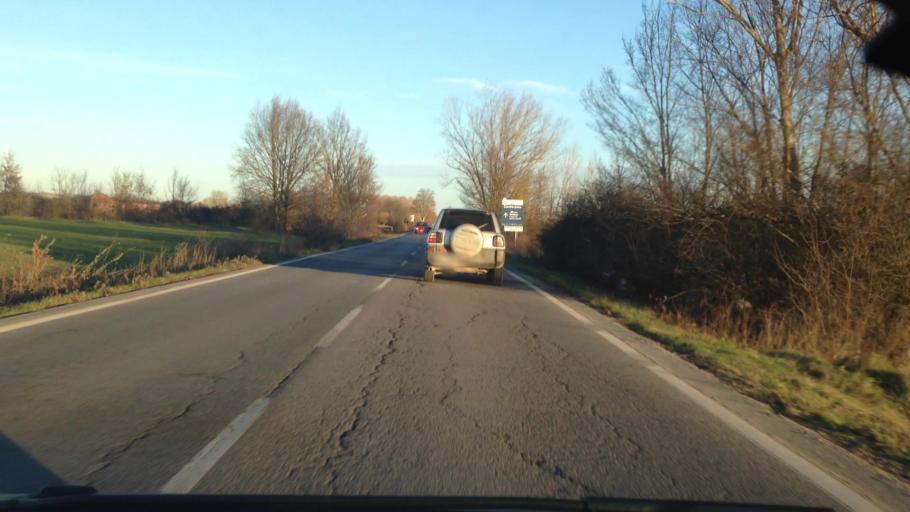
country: IT
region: Piedmont
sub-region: Provincia di Alessandria
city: Solero
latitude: 44.9211
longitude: 8.5324
